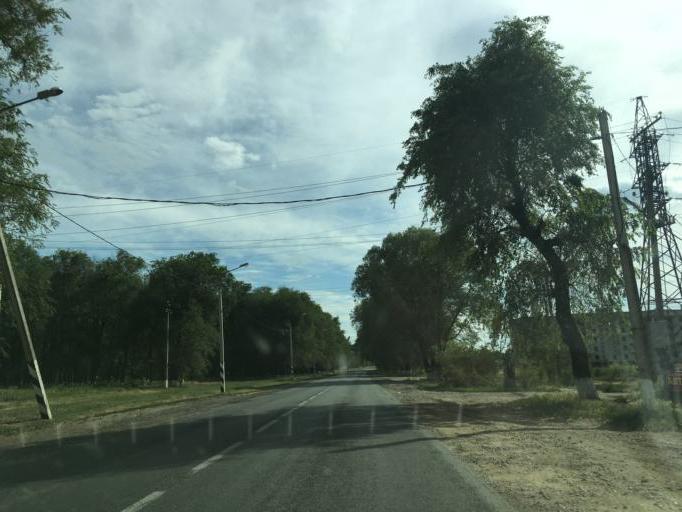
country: RU
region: Krasnodarskiy
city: Kushchevskaya
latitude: 46.5432
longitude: 39.6213
